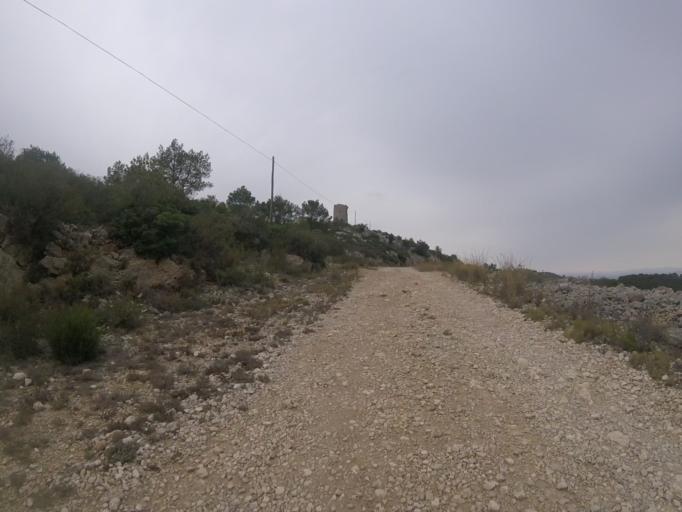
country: ES
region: Valencia
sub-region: Provincia de Castello
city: Alcoceber
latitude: 40.2794
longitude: 0.2831
